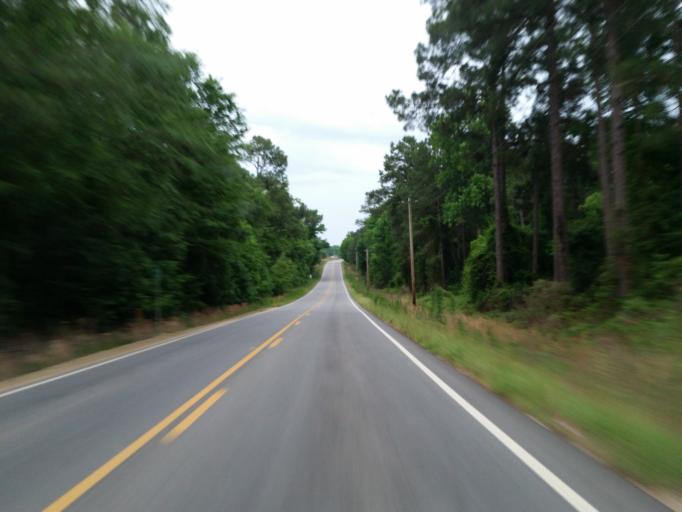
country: US
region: Georgia
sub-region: Crisp County
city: Cordele
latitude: 31.8803
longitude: -83.7534
